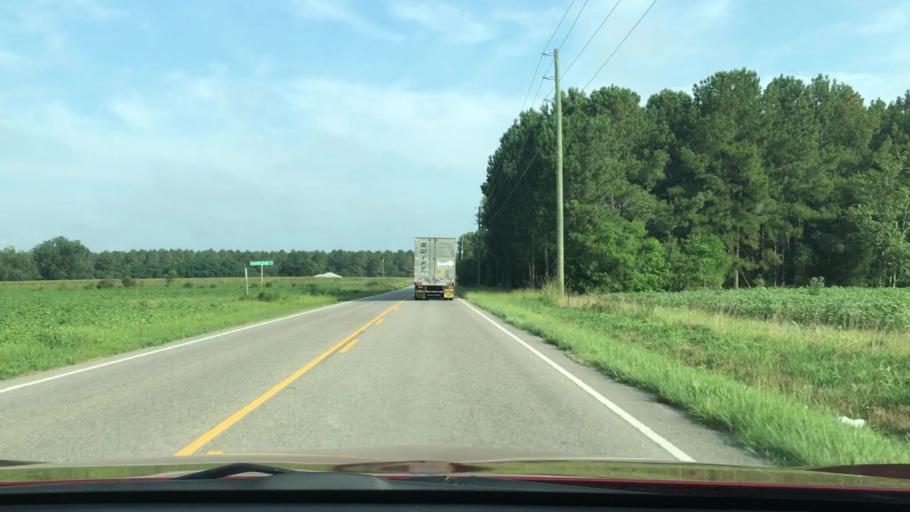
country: US
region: South Carolina
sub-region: Barnwell County
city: Blackville
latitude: 33.5980
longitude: -81.2594
